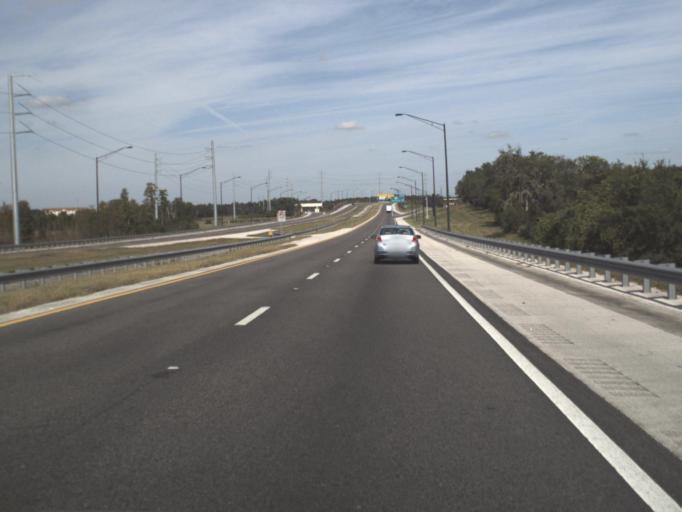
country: US
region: Florida
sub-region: Polk County
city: Citrus Ridge
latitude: 28.3369
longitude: -81.6155
